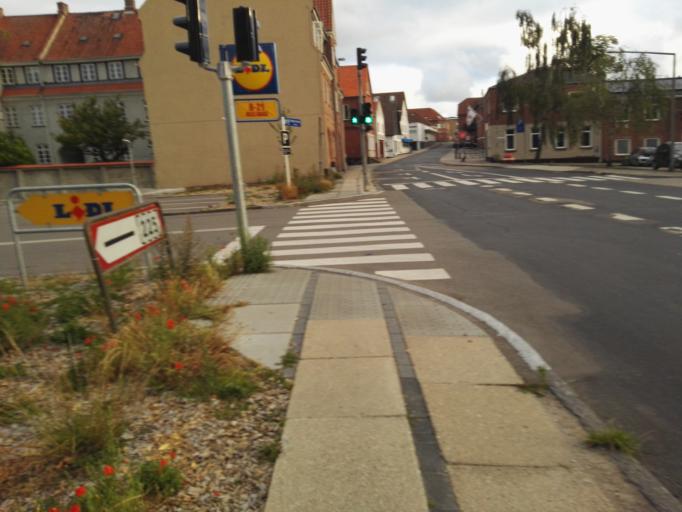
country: DK
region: Zealand
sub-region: Odsherred Kommune
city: Nykobing Sjaelland
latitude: 55.9211
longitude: 11.6717
